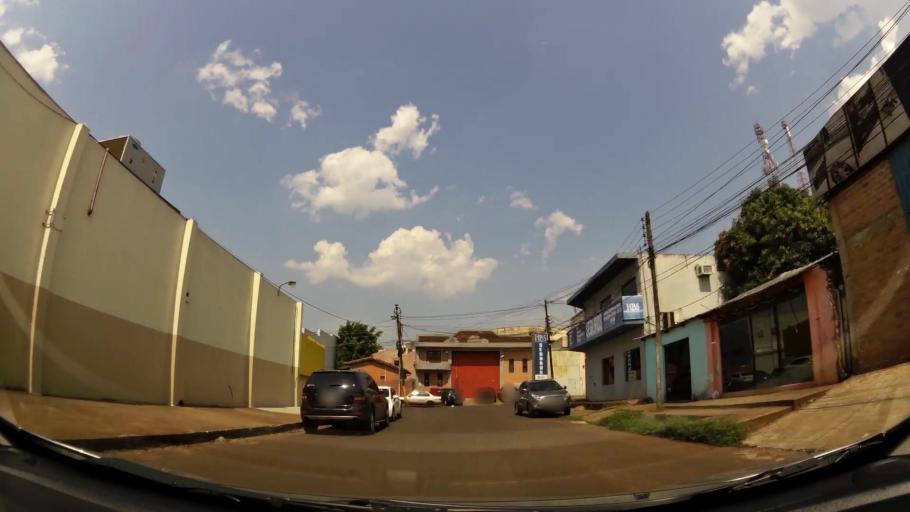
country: PY
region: Alto Parana
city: Ciudad del Este
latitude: -25.5088
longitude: -54.6378
